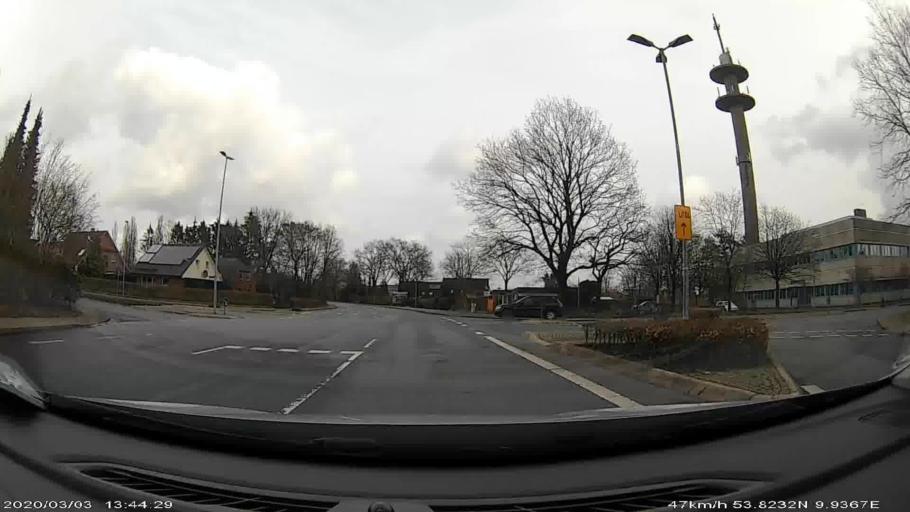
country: DE
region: Schleswig-Holstein
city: Kaltenkirchen
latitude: 53.8237
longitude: 9.9378
